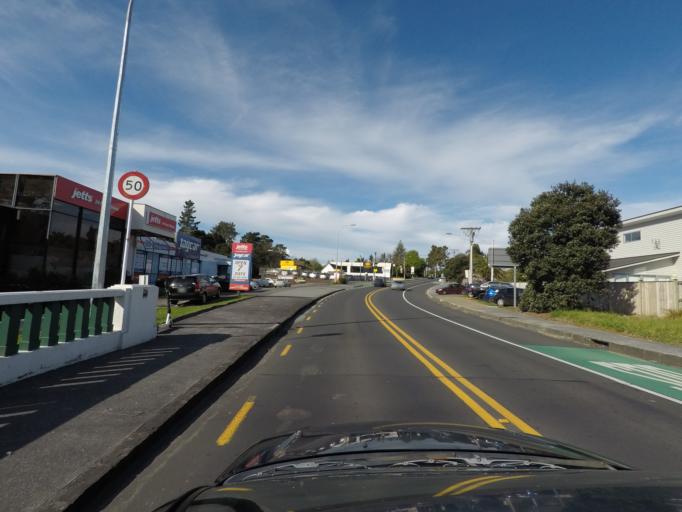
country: NZ
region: Auckland
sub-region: Auckland
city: Rosebank
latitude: -36.9028
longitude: 174.6898
